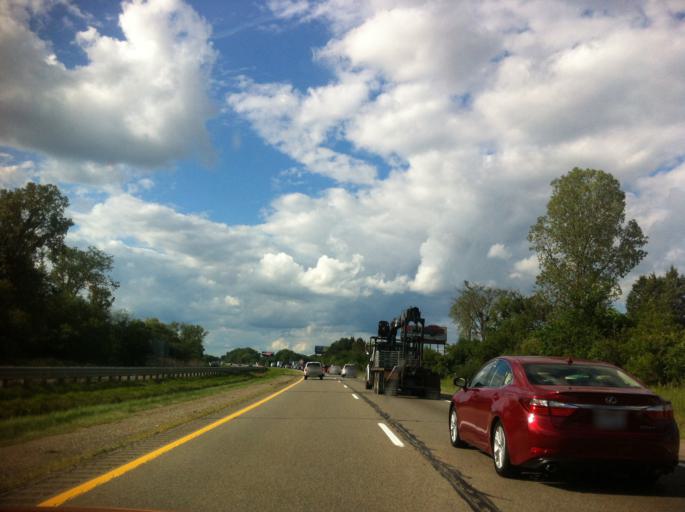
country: US
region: Michigan
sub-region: Livingston County
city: Whitmore Lake
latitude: 42.4067
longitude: -83.7626
